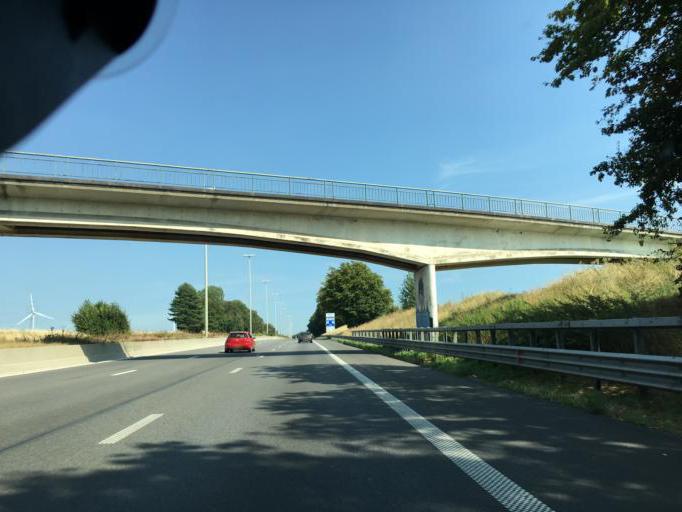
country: BE
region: Wallonia
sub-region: Province de Namur
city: Gembloux
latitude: 50.4942
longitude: 4.6811
